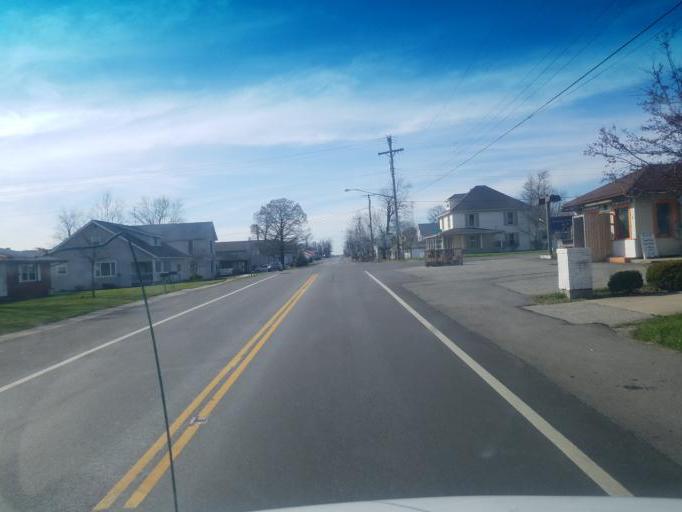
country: US
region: Ohio
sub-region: Union County
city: Marysville
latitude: 40.3332
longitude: -83.4646
